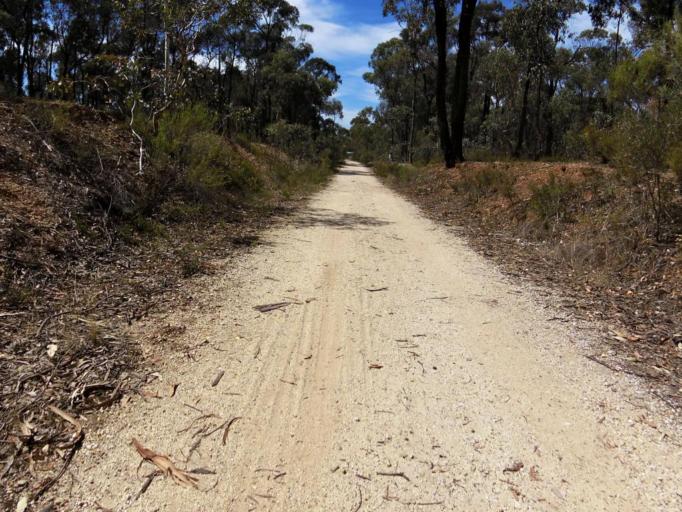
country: AU
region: Victoria
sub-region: Greater Bendigo
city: Kennington
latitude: -36.7606
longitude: 144.3360
